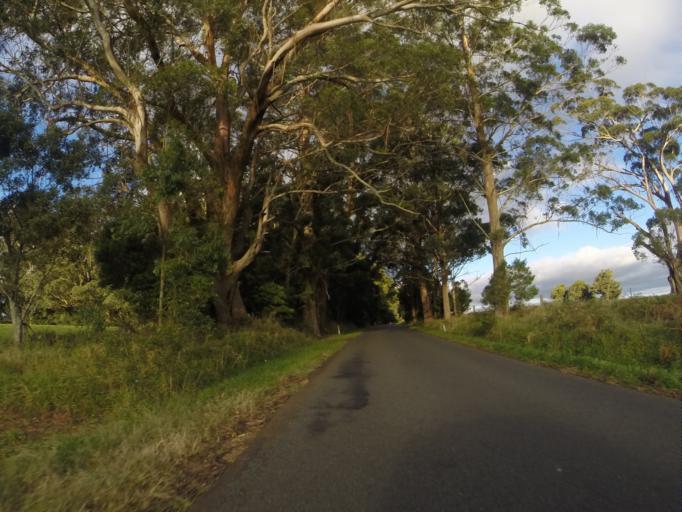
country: AU
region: New South Wales
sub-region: Shoalhaven Shire
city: Kangaroo Valley
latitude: -34.6072
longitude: 150.5392
